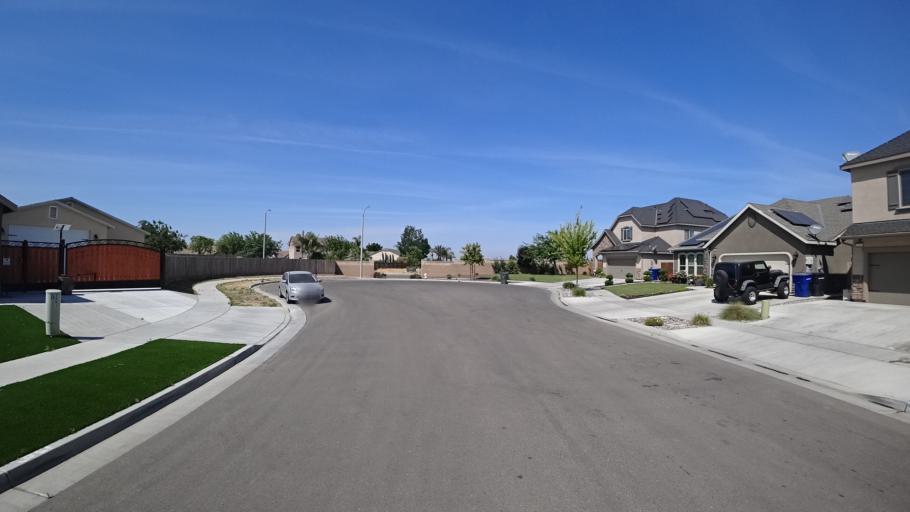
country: US
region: California
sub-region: Kings County
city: Armona
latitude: 36.3357
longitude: -119.6798
